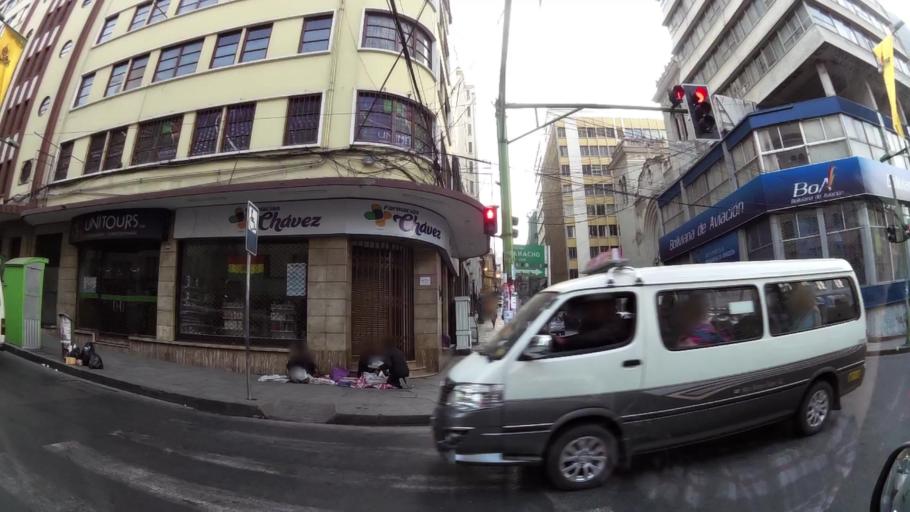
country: BO
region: La Paz
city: La Paz
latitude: -16.4993
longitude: -68.1334
